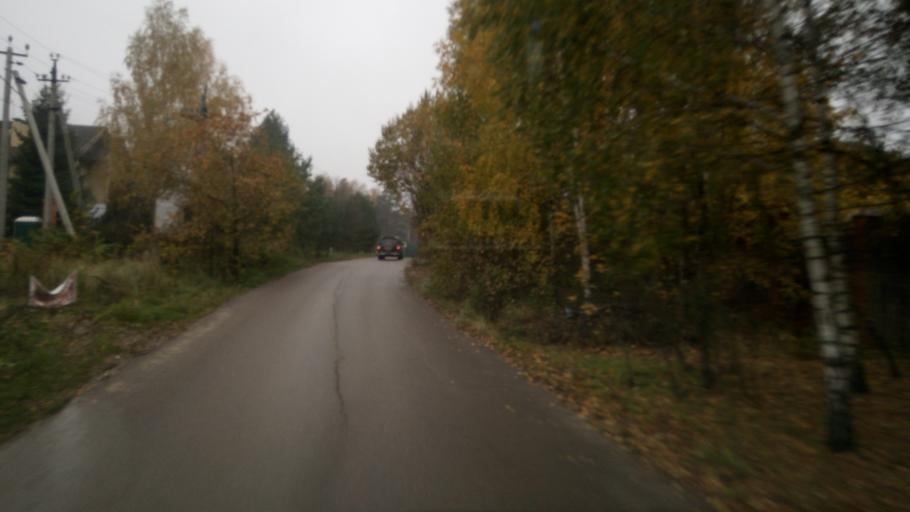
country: RU
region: Moskovskaya
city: Firsanovka
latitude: 55.9292
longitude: 37.2529
